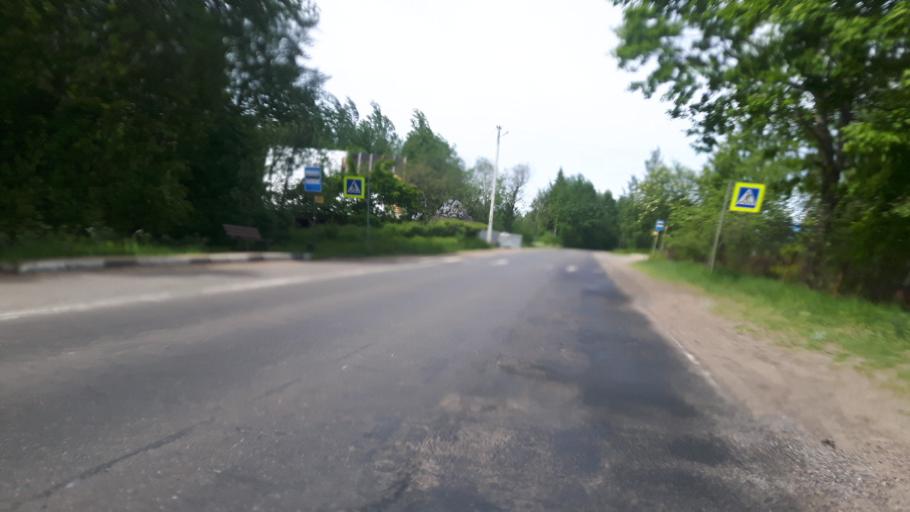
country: RU
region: Leningrad
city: Ust'-Luga
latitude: 59.6394
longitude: 28.2804
